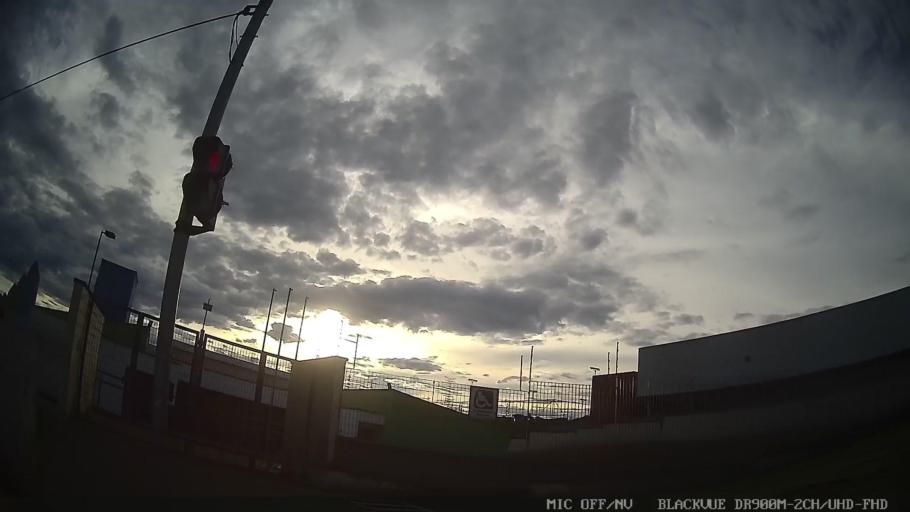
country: BR
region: Sao Paulo
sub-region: Mogi das Cruzes
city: Mogi das Cruzes
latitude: -23.5408
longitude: -46.1666
